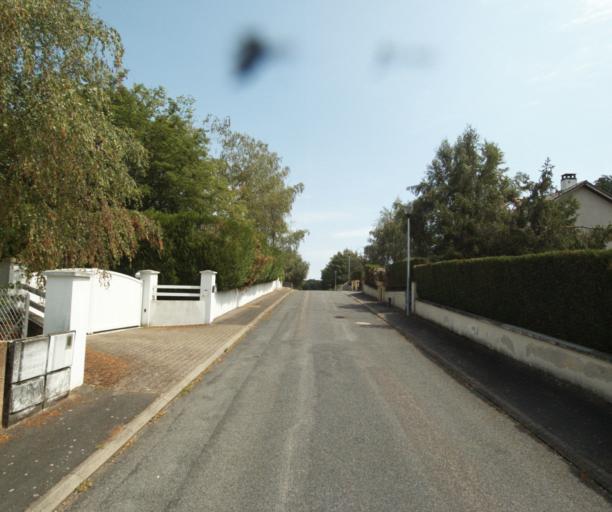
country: FR
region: Bourgogne
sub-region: Departement de Saone-et-Loire
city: Gueugnon
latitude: 46.5924
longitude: 4.0787
